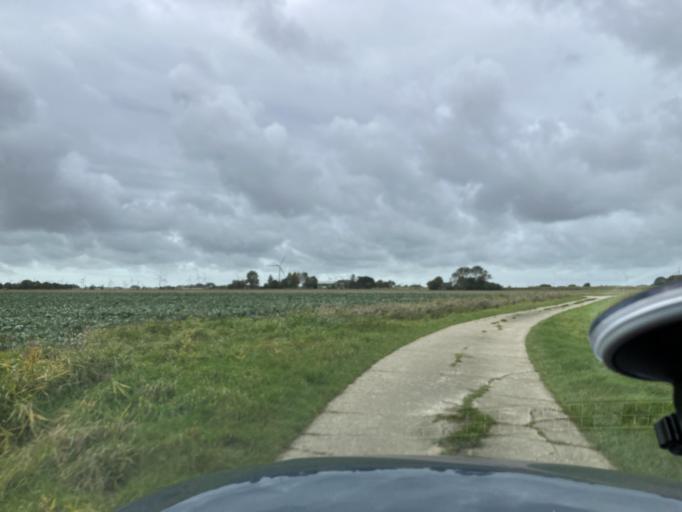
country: DE
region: Schleswig-Holstein
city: Norderwohrden
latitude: 54.2133
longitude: 9.0161
